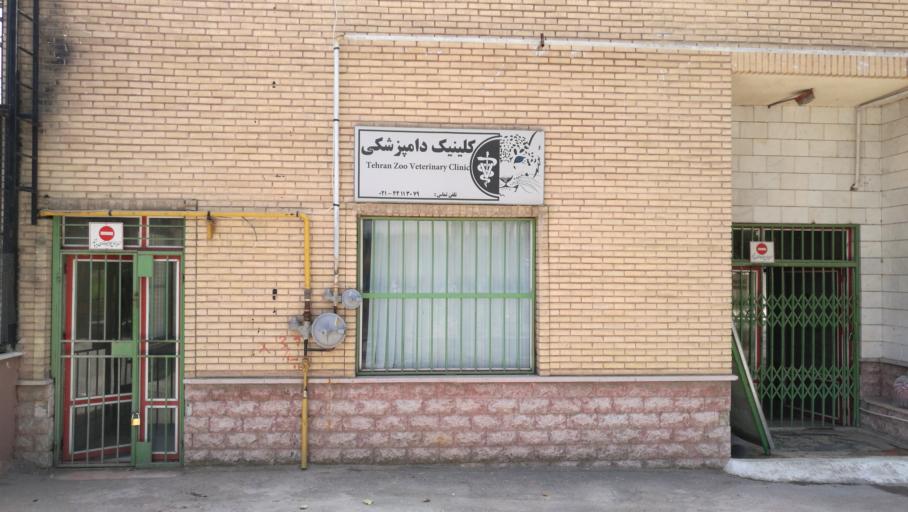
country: IR
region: Tehran
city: Tehran
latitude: 35.7197
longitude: 51.2924
